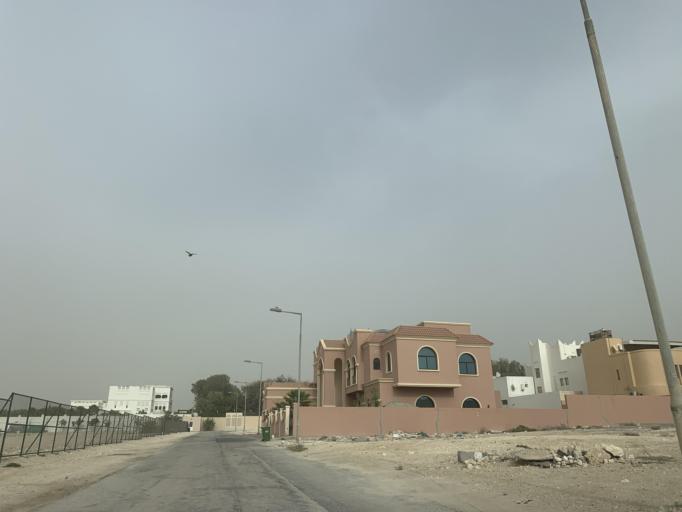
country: BH
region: Northern
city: Ar Rifa'
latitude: 26.1431
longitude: 50.5304
